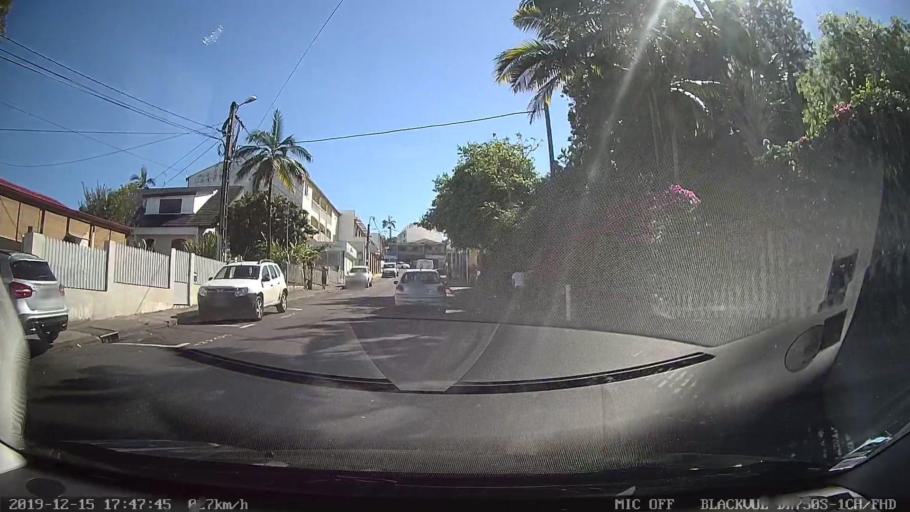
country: RE
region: Reunion
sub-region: Reunion
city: Le Tampon
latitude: -21.2796
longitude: 55.5144
